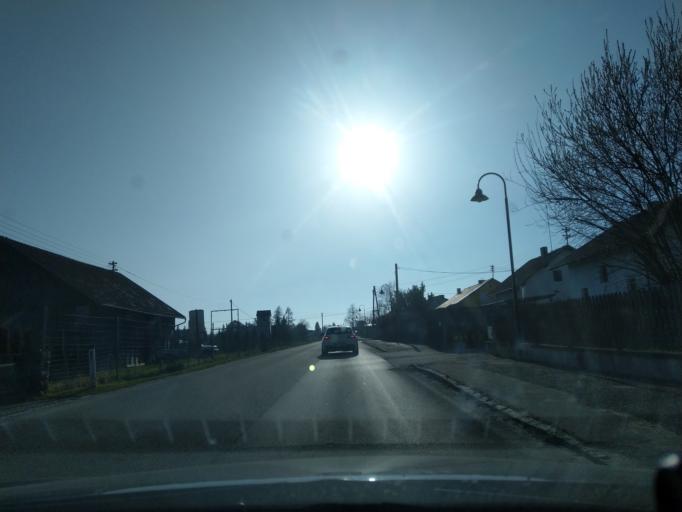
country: DE
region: Bavaria
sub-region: Lower Bavaria
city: Bad Fussing
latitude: 48.3170
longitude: 13.3271
